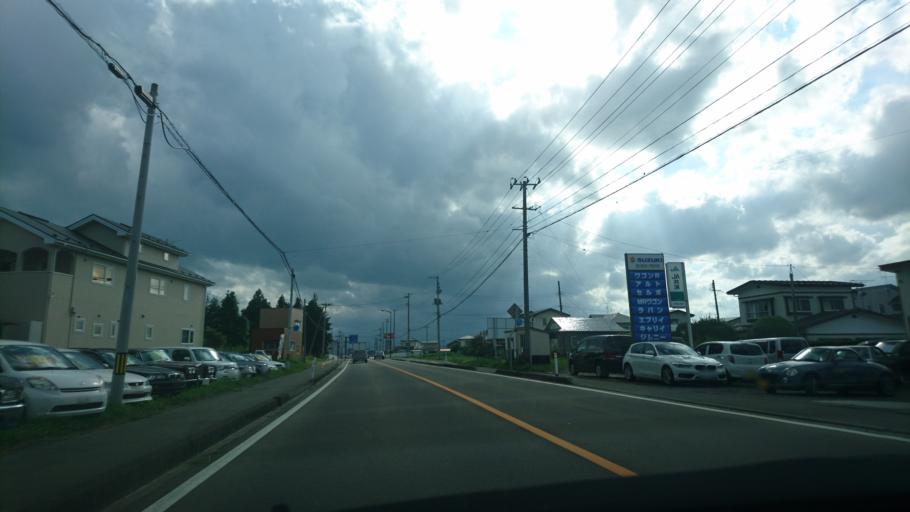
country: JP
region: Iwate
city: Hanamaki
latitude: 39.3904
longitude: 141.1487
